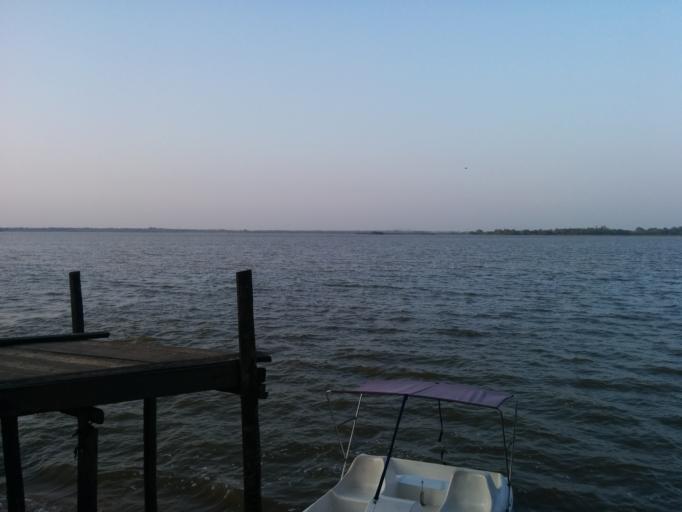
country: IN
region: Pondicherry
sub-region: Puducherry
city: Puducherry
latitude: 11.9416
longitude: 79.7469
